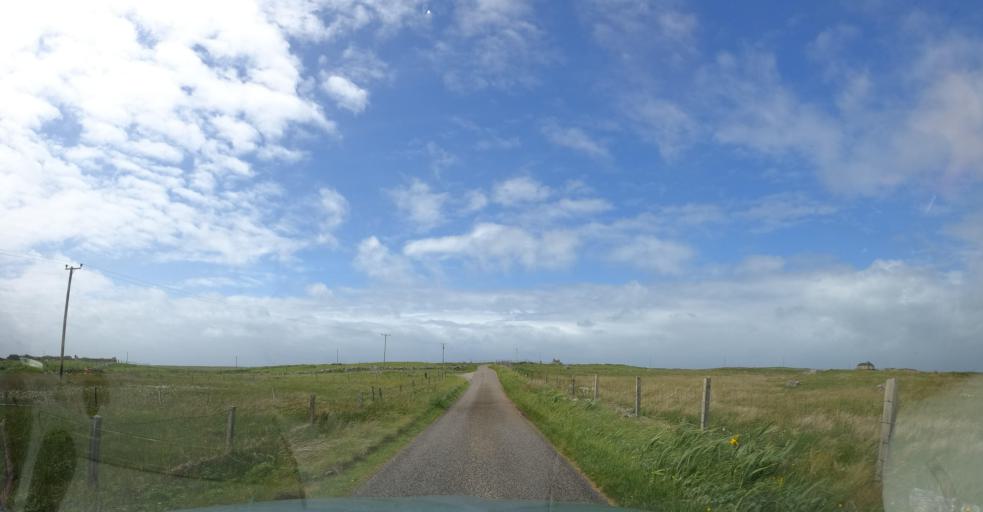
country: GB
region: Scotland
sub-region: Eilean Siar
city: Isle of South Uist
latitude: 57.2734
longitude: -7.4050
